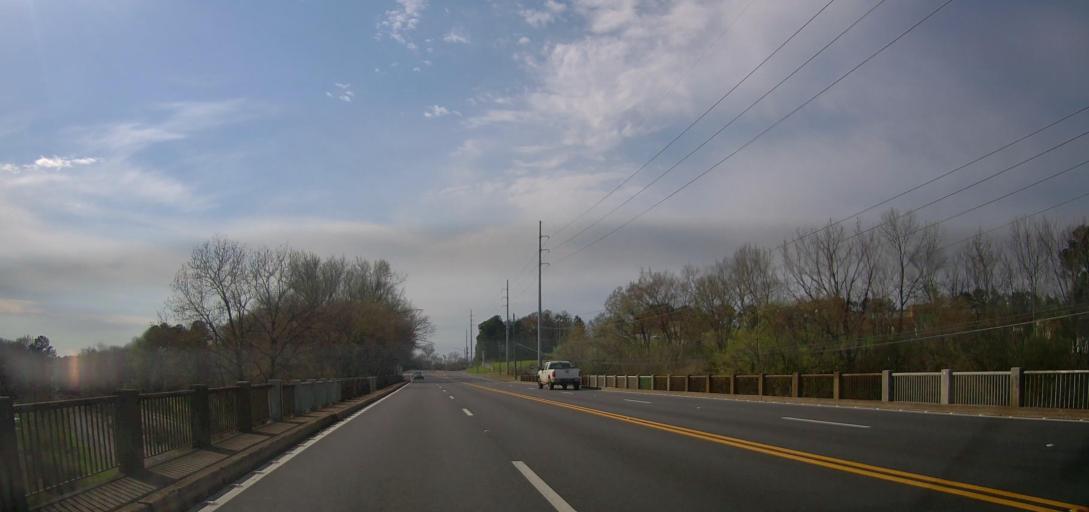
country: US
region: Alabama
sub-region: Jefferson County
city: Forestdale
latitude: 33.5340
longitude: -86.8608
